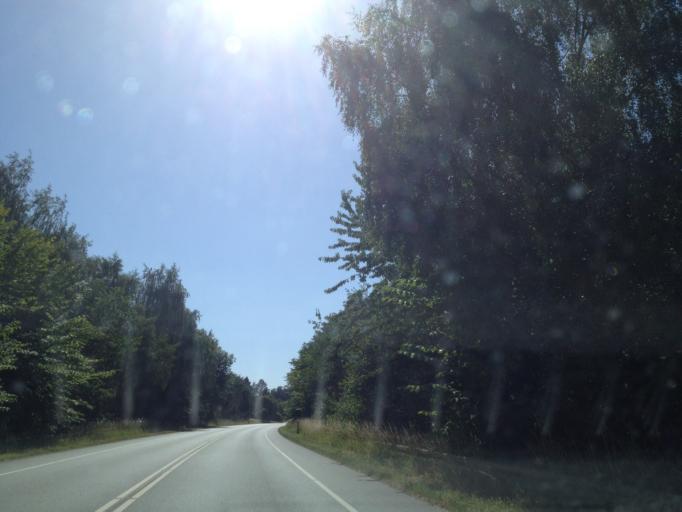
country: DK
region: Capital Region
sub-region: Hillerod Kommune
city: Nodebo
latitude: 56.0413
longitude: 12.3545
